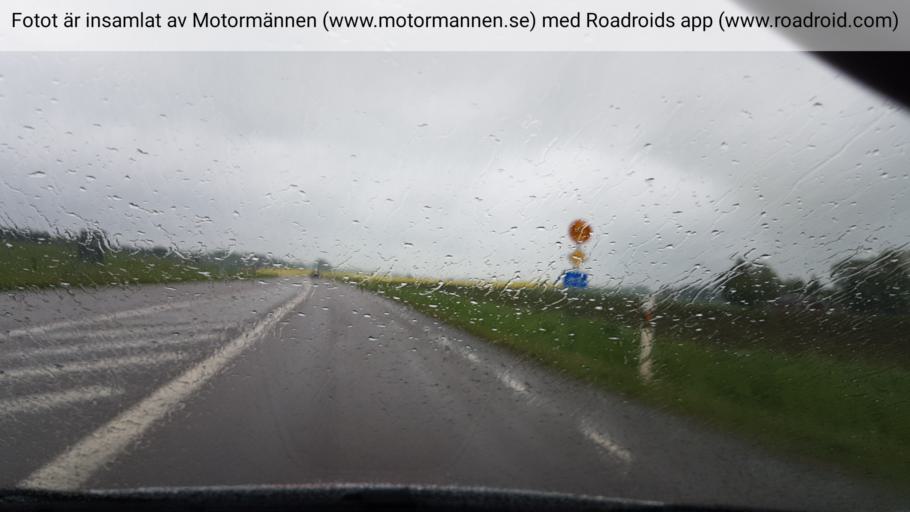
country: SE
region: Vaestra Goetaland
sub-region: Falkopings Kommun
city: Falkoeping
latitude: 58.1350
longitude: 13.5624
